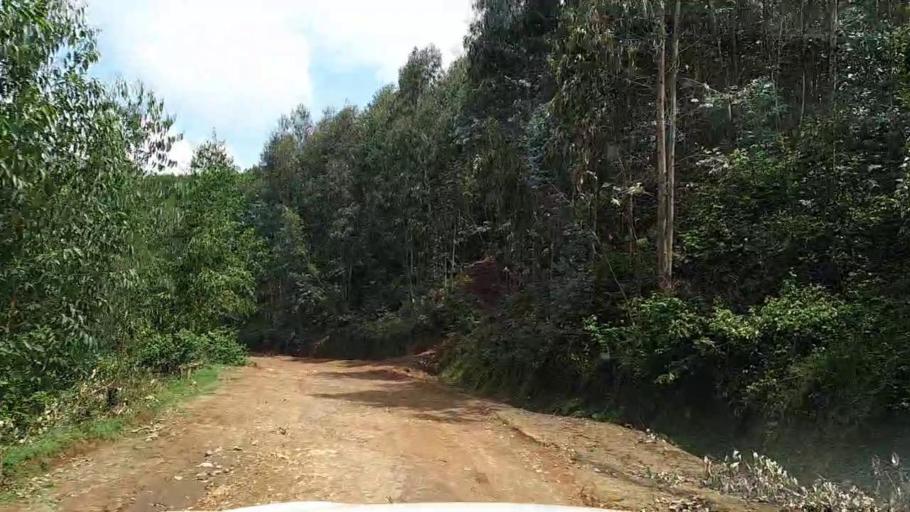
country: RW
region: Southern Province
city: Gikongoro
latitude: -2.3400
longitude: 29.5152
